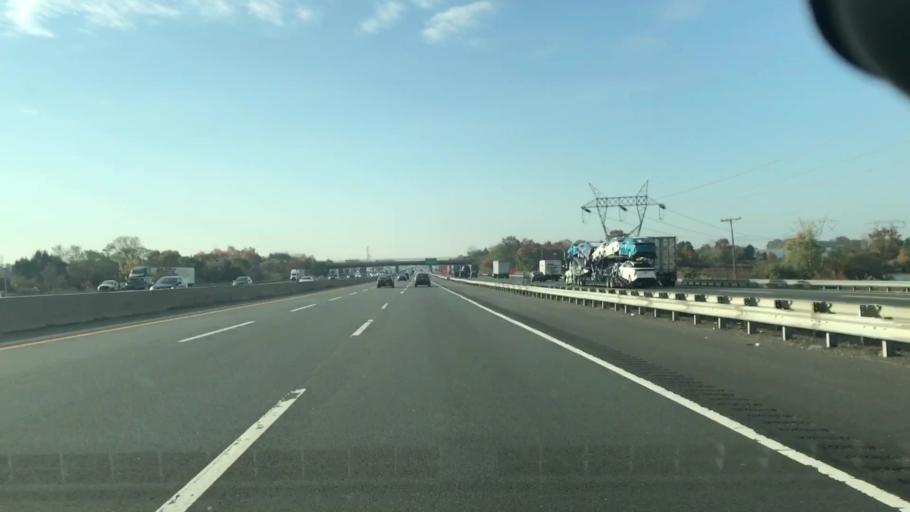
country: US
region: New Jersey
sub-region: Middlesex County
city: Jamesburg
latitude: 40.3789
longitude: -74.4626
